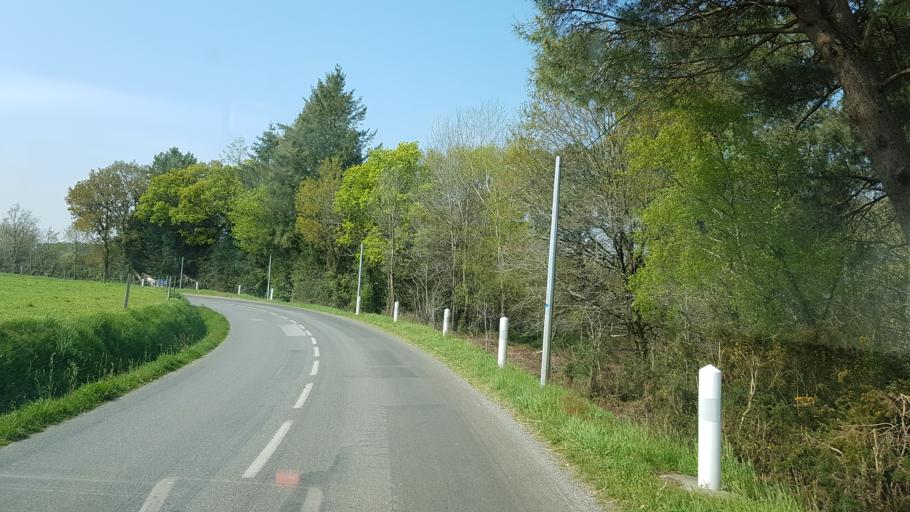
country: FR
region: Brittany
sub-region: Departement du Morbihan
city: Caden
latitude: 47.5940
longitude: -2.2914
